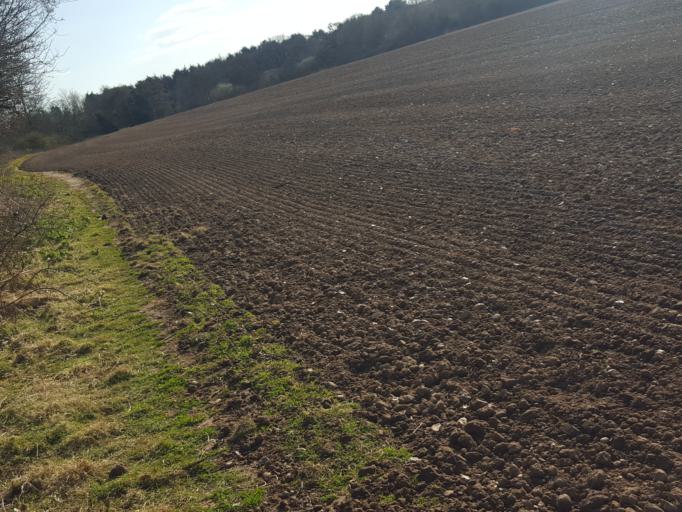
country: GB
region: England
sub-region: Essex
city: Little Clacton
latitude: 51.8653
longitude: 1.1142
